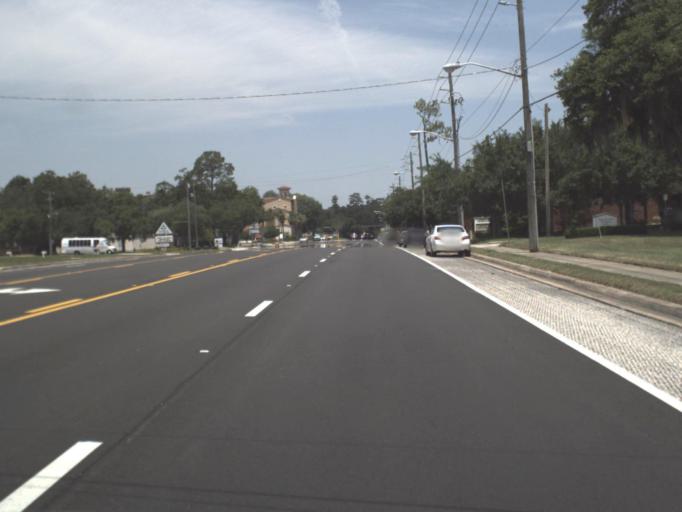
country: US
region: Florida
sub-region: Duval County
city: Jacksonville
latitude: 30.2575
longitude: -81.6432
